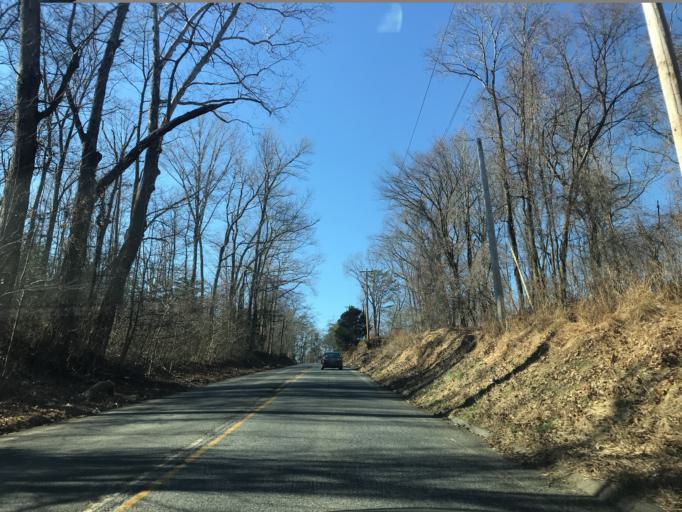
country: US
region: Maryland
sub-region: Charles County
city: Bryans Road
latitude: 38.6017
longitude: -77.0612
